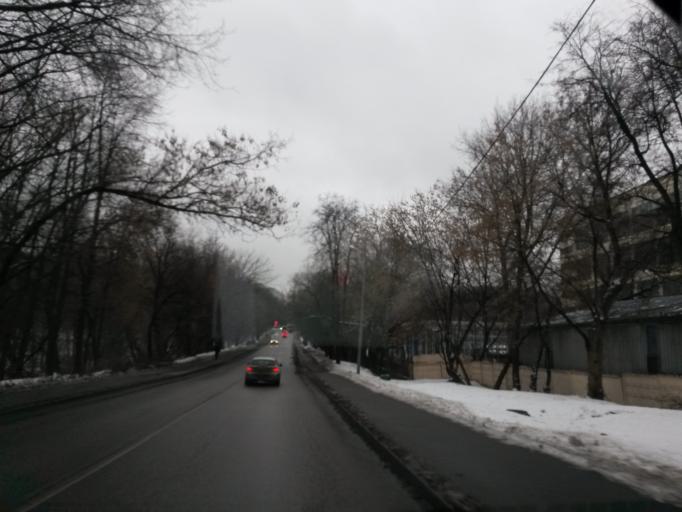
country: RU
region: Moskovskaya
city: Bol'shaya Setun'
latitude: 55.7144
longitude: 37.4377
